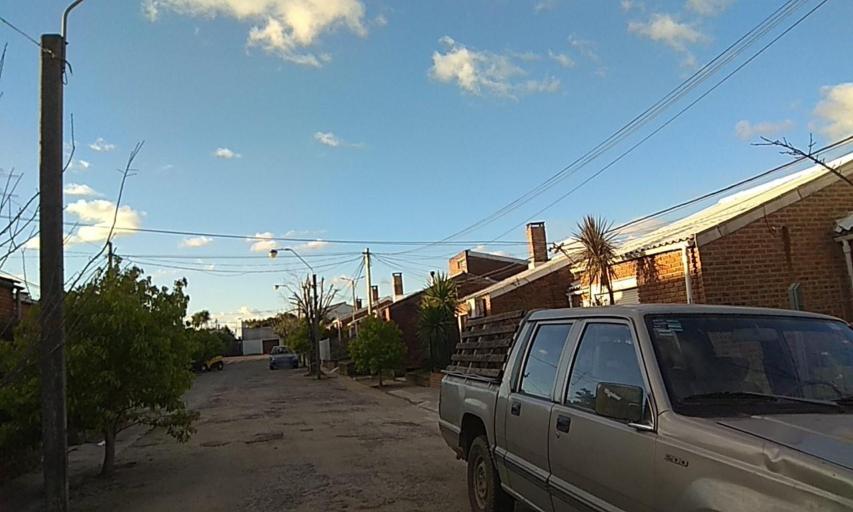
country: UY
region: Florida
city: Florida
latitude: -34.1026
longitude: -56.2294
